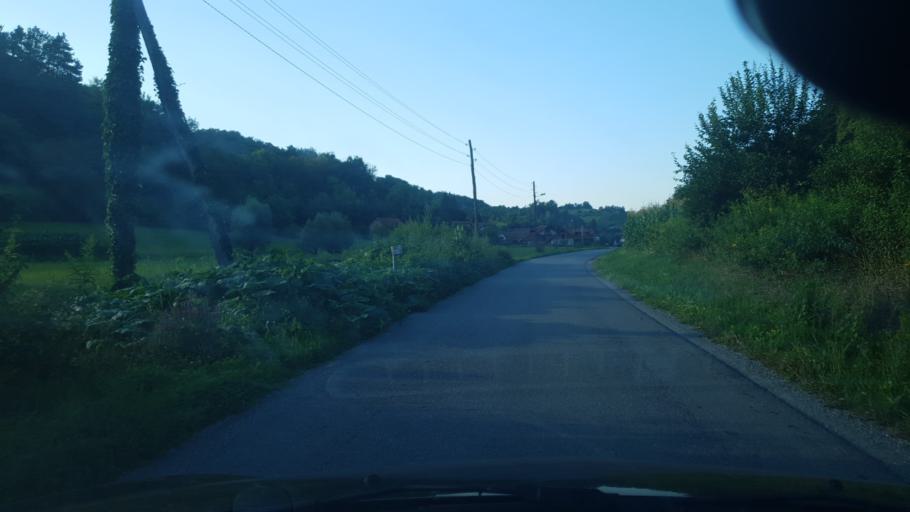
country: HR
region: Krapinsko-Zagorska
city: Zabok
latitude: 46.0525
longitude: 15.8876
